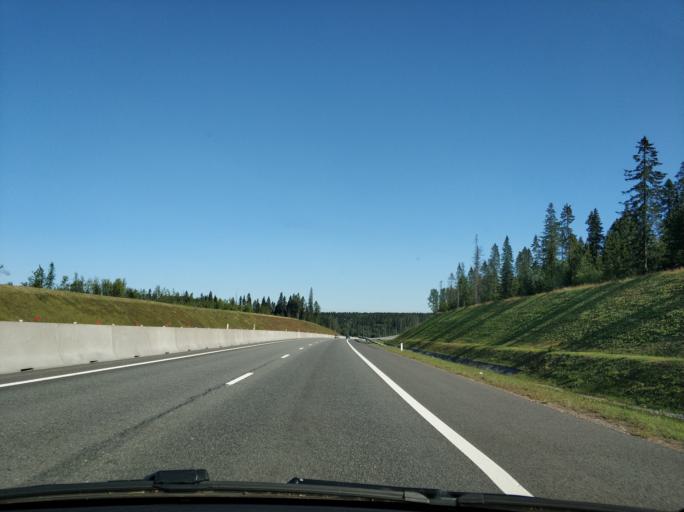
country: RU
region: Leningrad
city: Sosnovo
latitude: 60.4509
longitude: 30.1997
